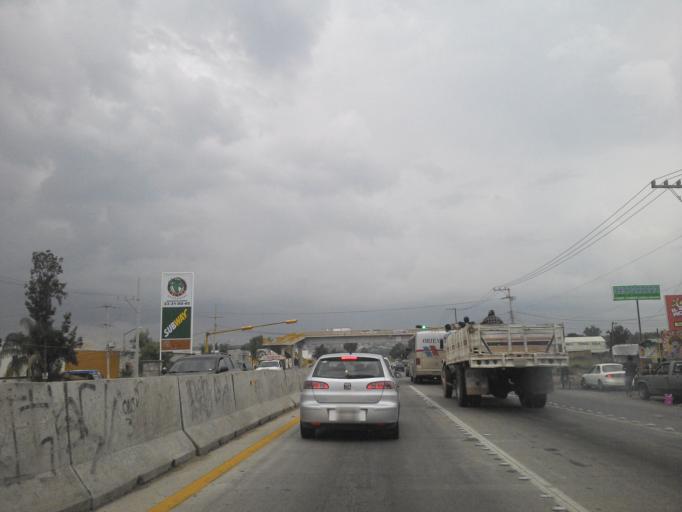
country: MX
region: Jalisco
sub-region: Tonala
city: Colonia Guadalupana
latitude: 20.5858
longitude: -103.2216
